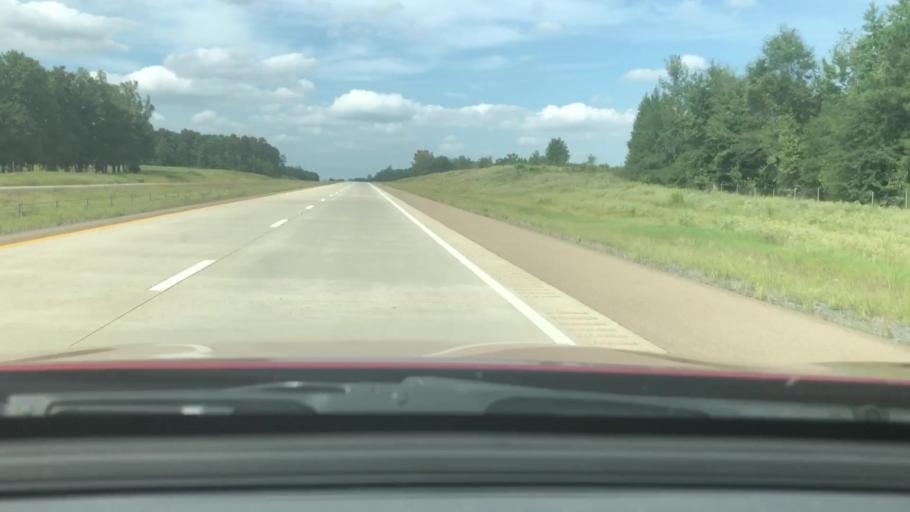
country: US
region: Louisiana
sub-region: Caddo Parish
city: Vivian
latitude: 33.0394
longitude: -93.8998
